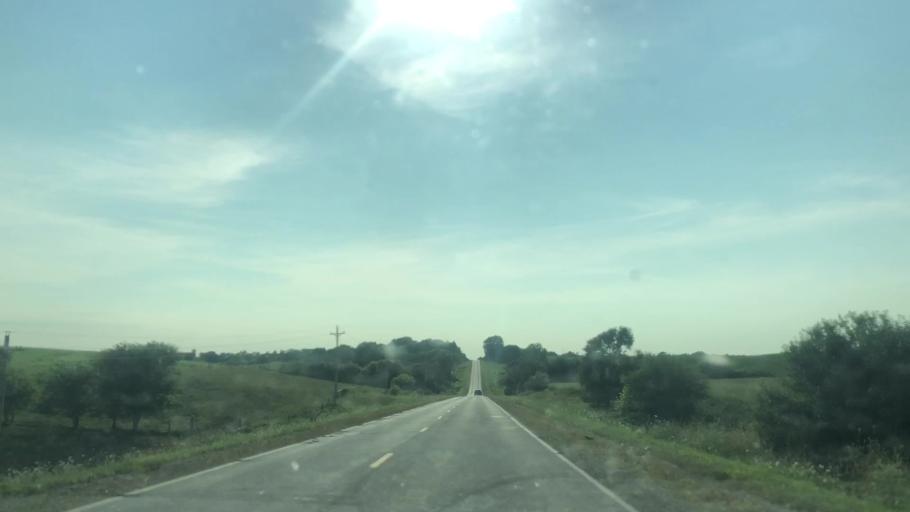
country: US
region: Iowa
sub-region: Marshall County
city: Marshalltown
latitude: 42.0490
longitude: -92.9660
